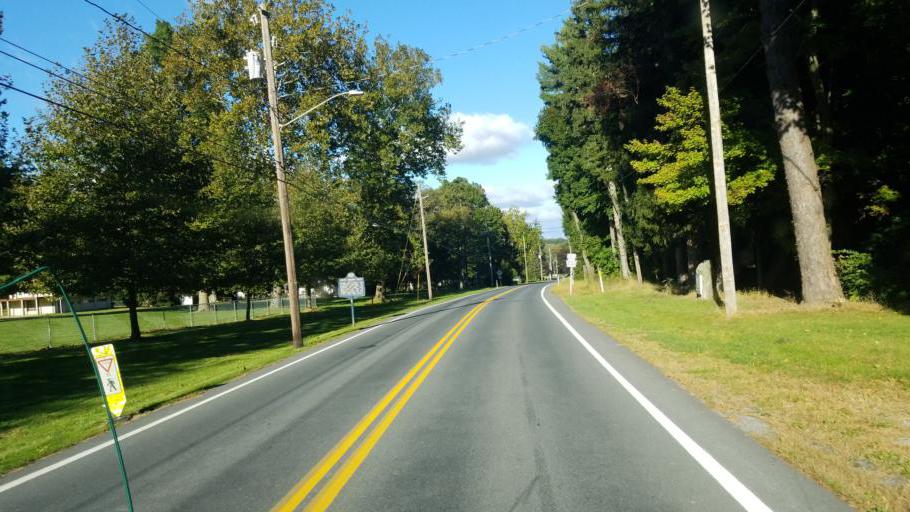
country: US
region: Pennsylvania
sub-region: Franklin County
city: Mont Alto
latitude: 39.8402
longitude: -77.5446
